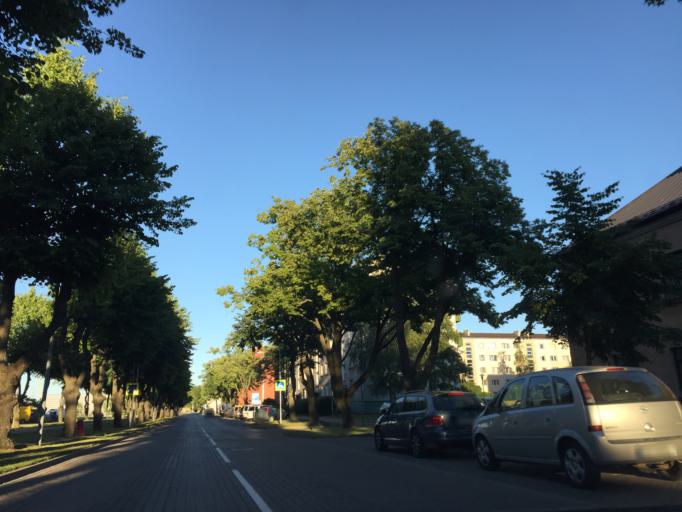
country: LV
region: Ventspils
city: Ventspils
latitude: 57.3911
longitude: 21.5780
